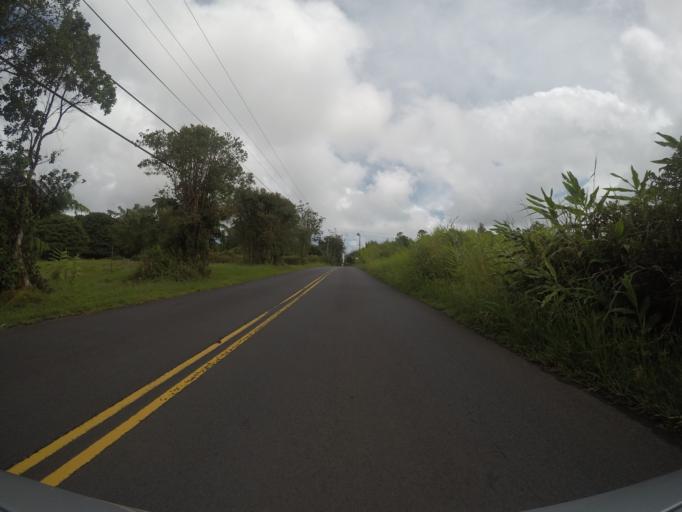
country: US
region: Hawaii
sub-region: Hawaii County
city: Fern Acres
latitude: 19.4855
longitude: -155.1516
